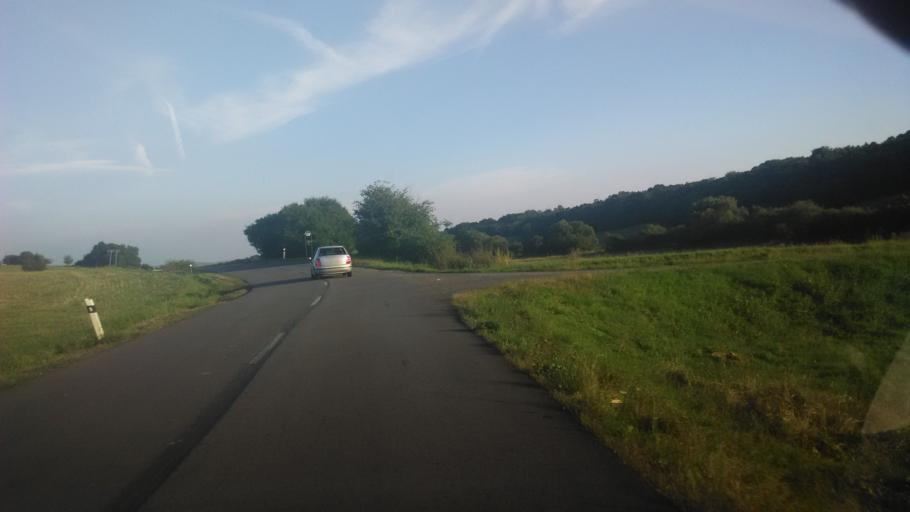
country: SK
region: Banskobystricky
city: Dudince
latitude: 48.2086
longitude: 18.7897
